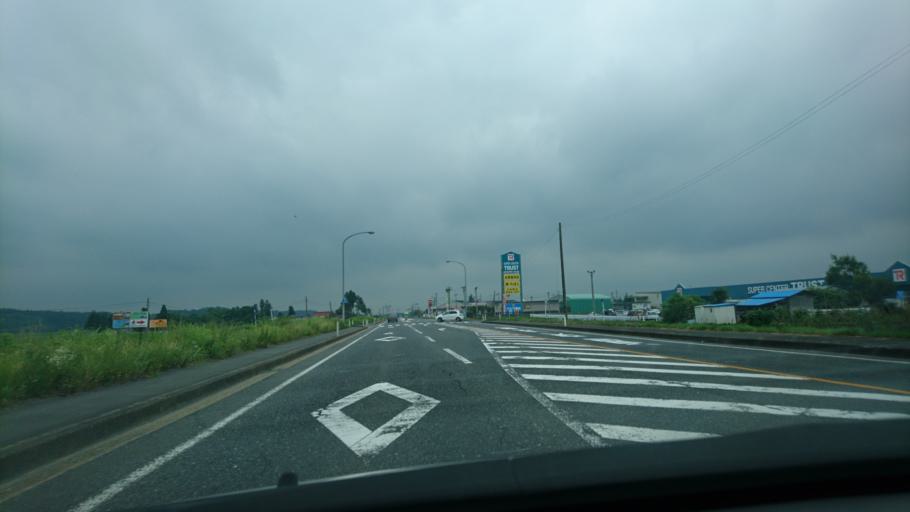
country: JP
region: Miyagi
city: Furukawa
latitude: 38.6694
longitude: 140.8670
